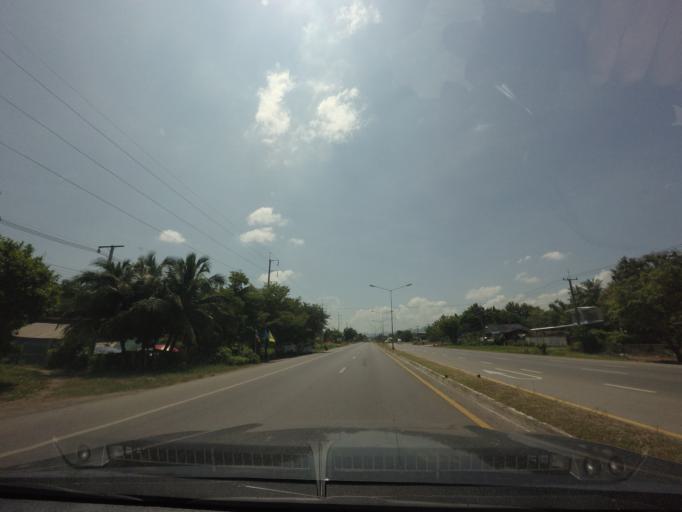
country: TH
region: Phetchabun
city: Lom Sak
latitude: 16.7063
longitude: 101.1757
